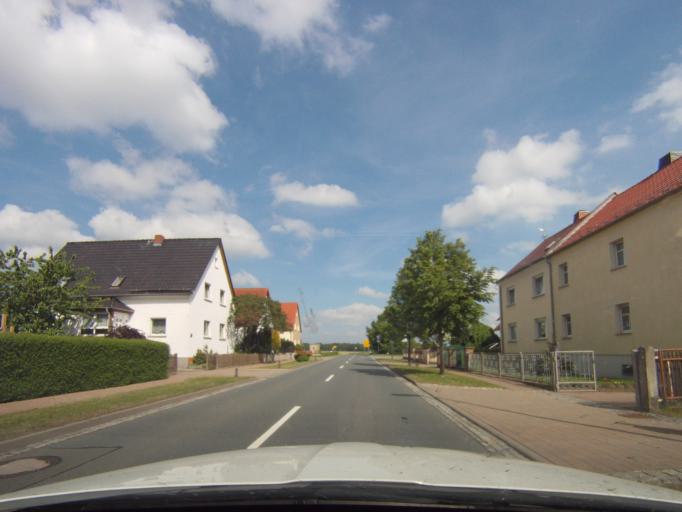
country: DE
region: Thuringia
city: Renthendorf
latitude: 50.7860
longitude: 11.9597
